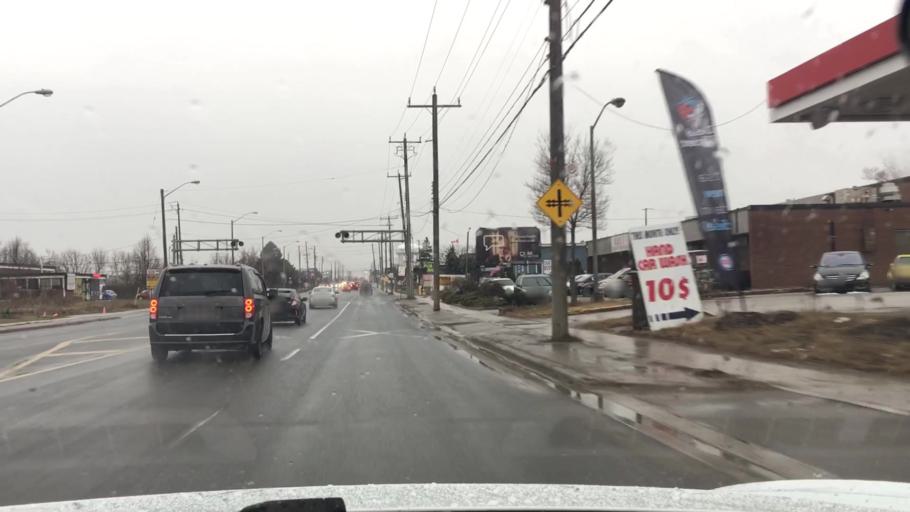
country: CA
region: Ontario
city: Scarborough
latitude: 43.7185
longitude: -79.2836
